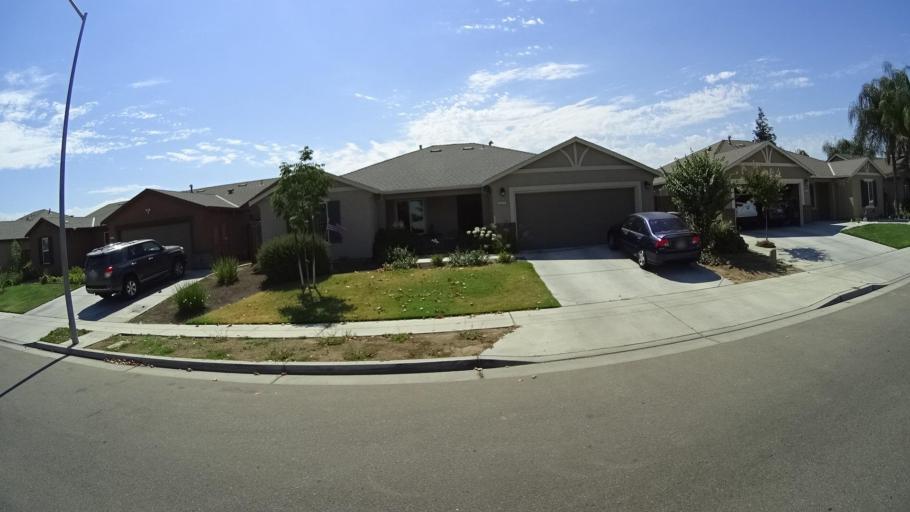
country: US
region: California
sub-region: Fresno County
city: Sunnyside
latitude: 36.7142
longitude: -119.7091
